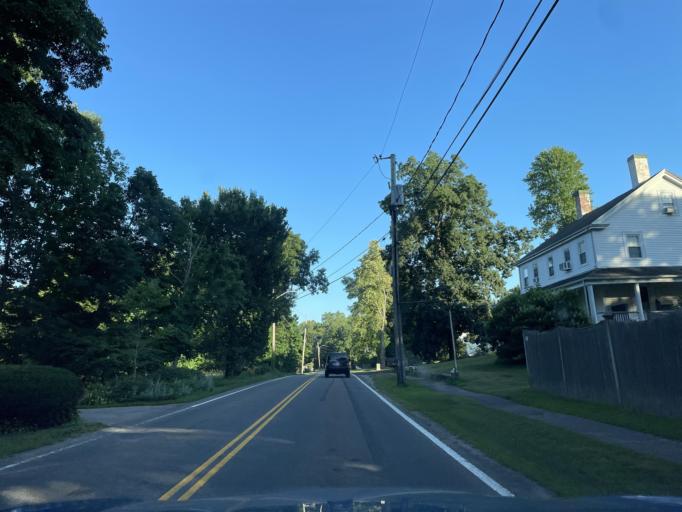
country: US
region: Massachusetts
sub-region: Plymouth County
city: East Bridgewater
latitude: 42.0133
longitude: -70.9614
